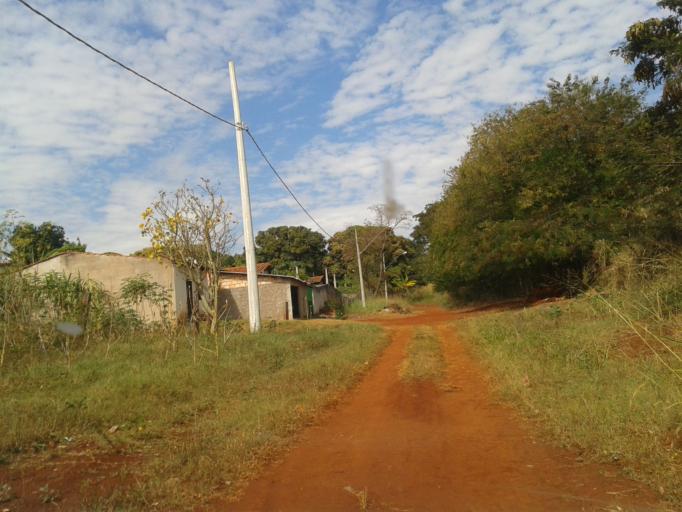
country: BR
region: Minas Gerais
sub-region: Ituiutaba
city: Ituiutaba
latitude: -18.9464
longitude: -49.4625
